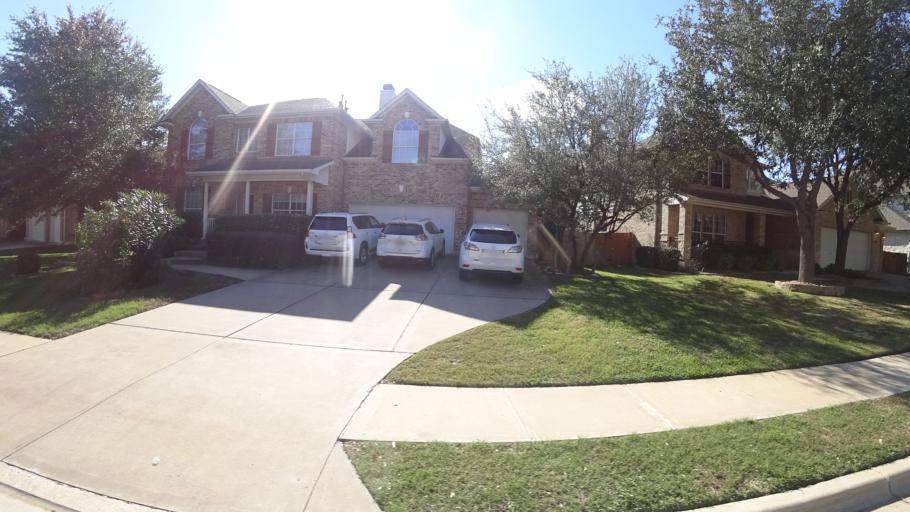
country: US
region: Texas
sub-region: Travis County
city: Hudson Bend
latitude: 30.3794
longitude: -97.9032
